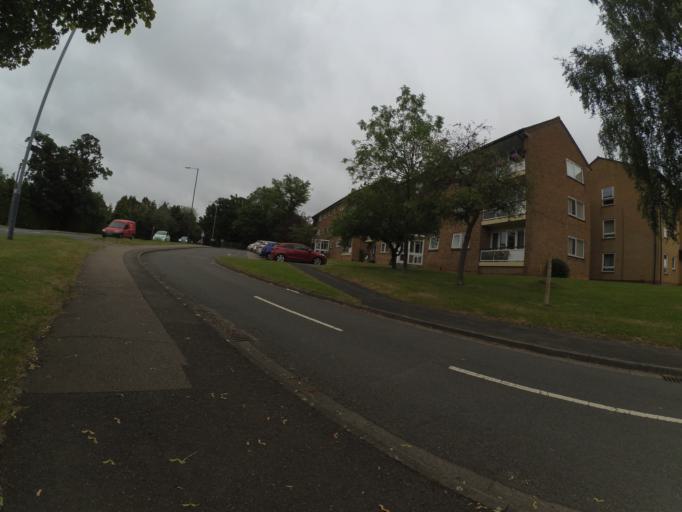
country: GB
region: England
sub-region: Warwickshire
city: Rugby
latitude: 52.3557
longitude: -1.2705
